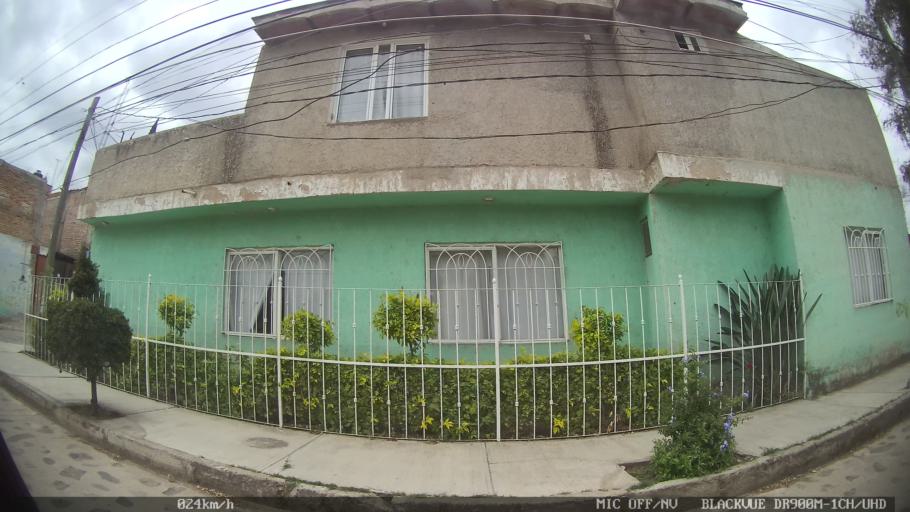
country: MX
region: Jalisco
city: Tonala
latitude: 20.6445
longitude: -103.2507
